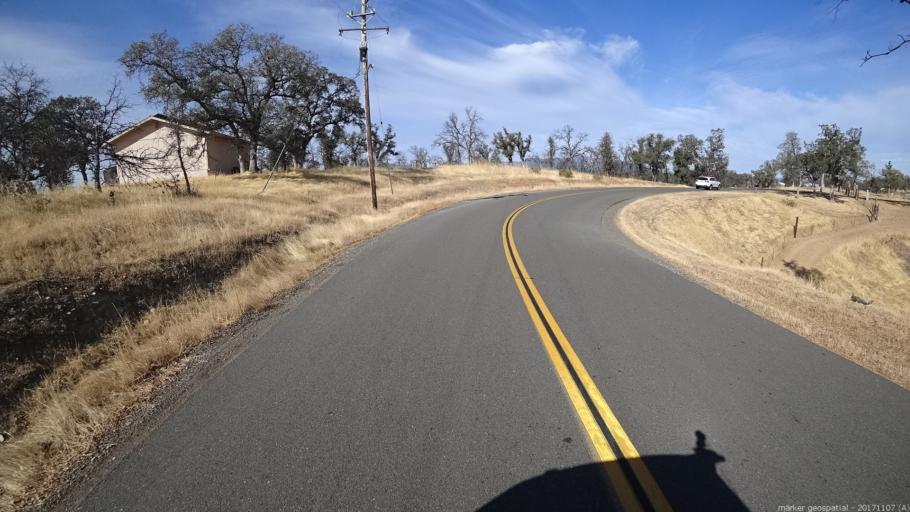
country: US
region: California
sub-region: Shasta County
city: Shasta
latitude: 40.4495
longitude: -122.5318
